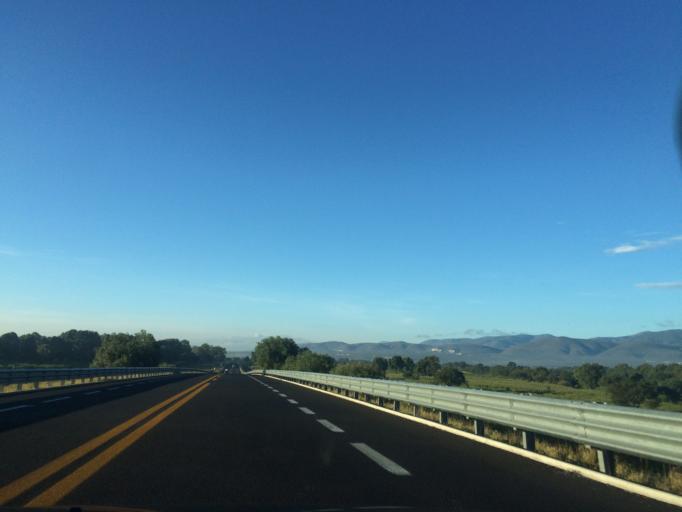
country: MX
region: Puebla
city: Santiago Miahuatlan
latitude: 18.5326
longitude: -97.4577
